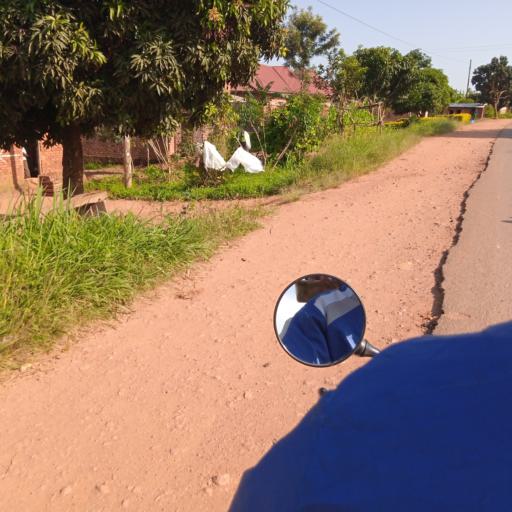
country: UG
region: Central Region
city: Masaka
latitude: -0.4376
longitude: 31.6628
